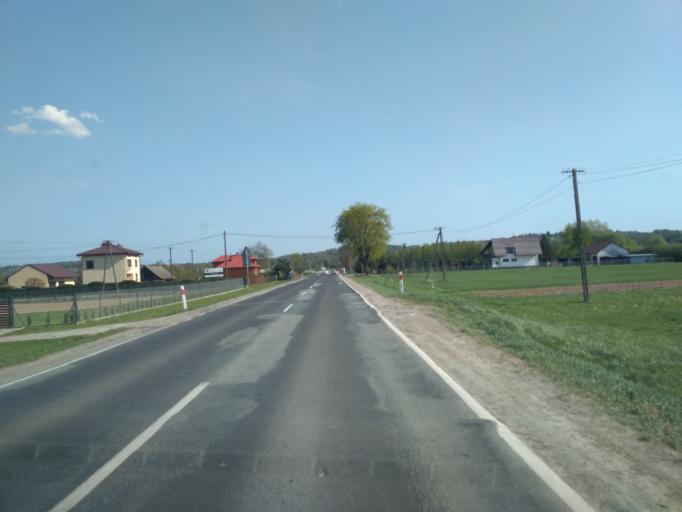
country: PL
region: Subcarpathian Voivodeship
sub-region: Powiat jasielski
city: Trzcinica
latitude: 49.7287
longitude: 21.4115
